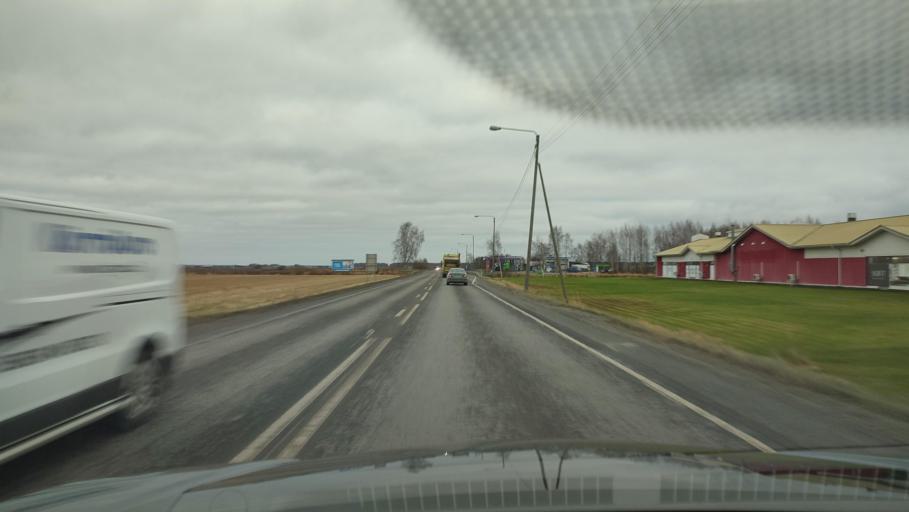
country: FI
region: Southern Ostrobothnia
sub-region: Seinaejoki
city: Ilmajoki
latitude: 62.7318
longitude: 22.6017
